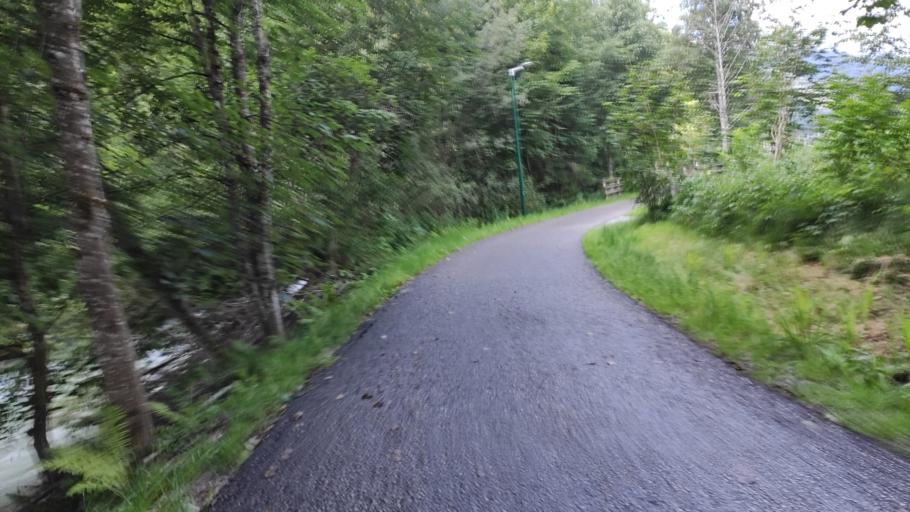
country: AT
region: Salzburg
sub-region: Politischer Bezirk Zell am See
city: Viehhofen
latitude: 47.3654
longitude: 12.7191
